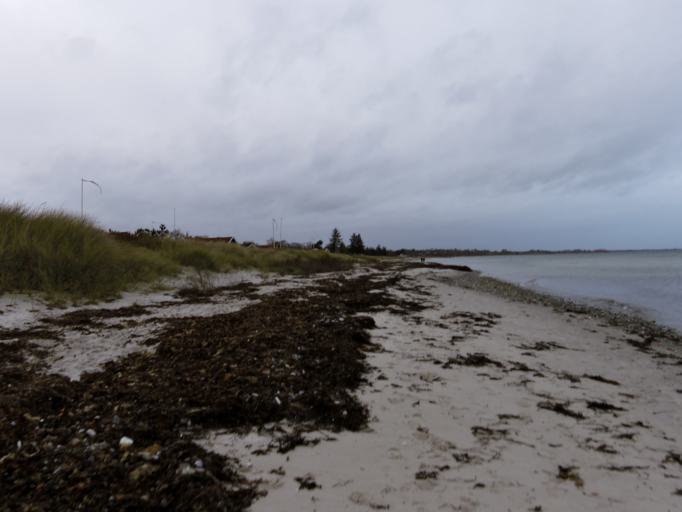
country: DK
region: Central Jutland
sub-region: Arhus Kommune
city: Malling
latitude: 55.9747
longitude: 10.2546
